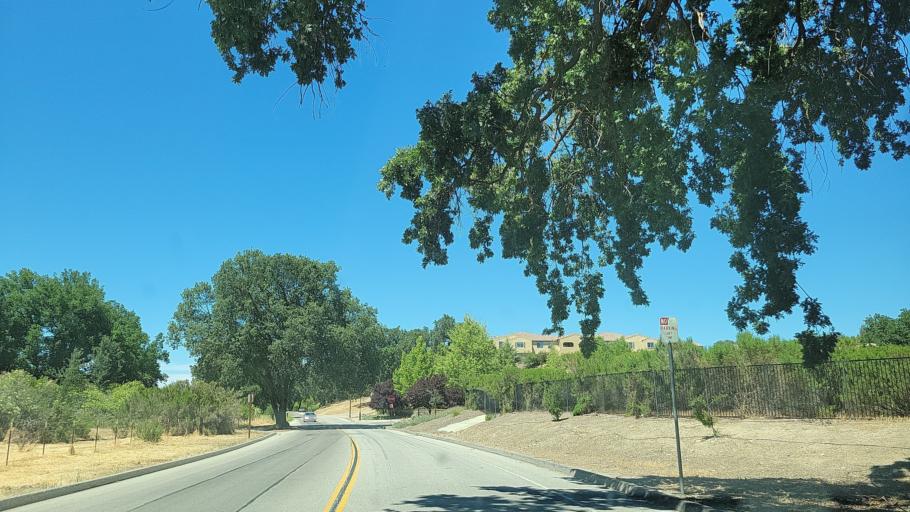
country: US
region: California
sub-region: San Luis Obispo County
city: Atascadero
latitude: 35.4541
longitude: -120.6320
